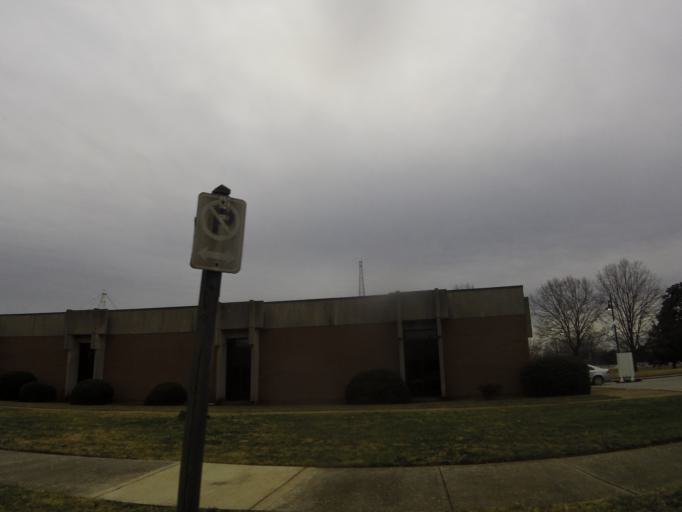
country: US
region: Virginia
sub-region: City of Portsmouth
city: Portsmouth
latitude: 36.8325
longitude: -76.2999
